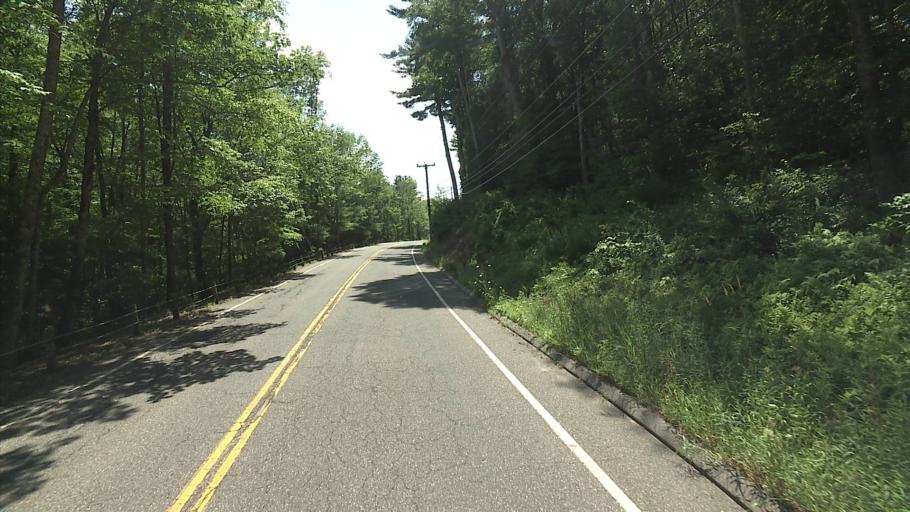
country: US
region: Connecticut
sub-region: Litchfield County
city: Canaan
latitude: 41.8692
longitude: -73.3292
